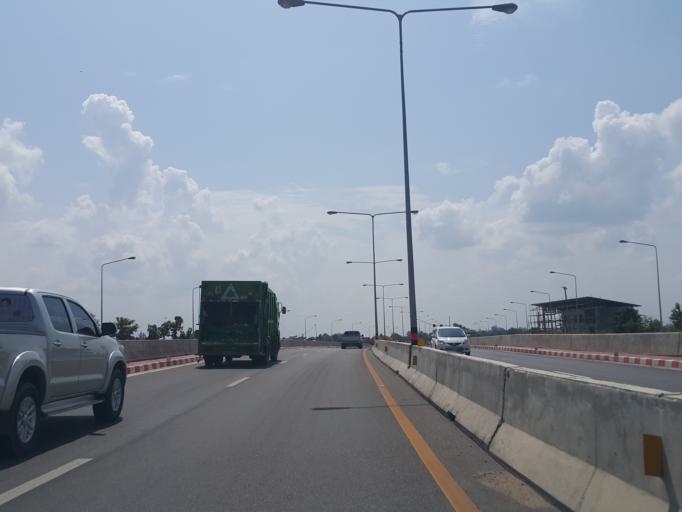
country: TH
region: Chiang Mai
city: Mae Wang
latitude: 18.6030
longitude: 98.8348
